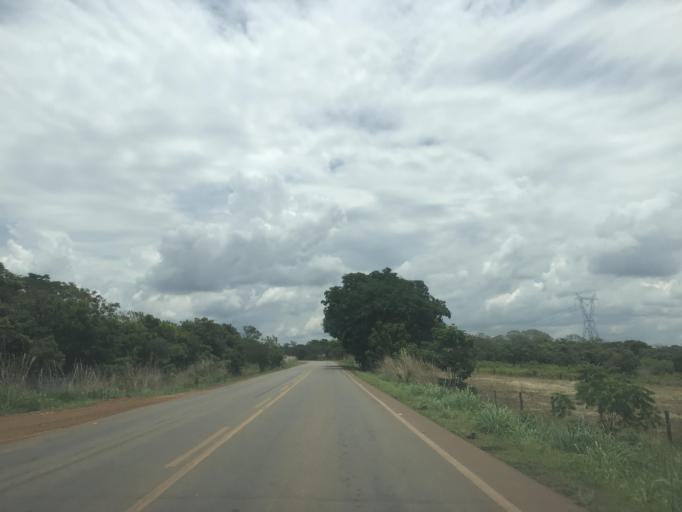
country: BR
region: Goias
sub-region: Vianopolis
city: Vianopolis
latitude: -16.7313
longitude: -48.4434
